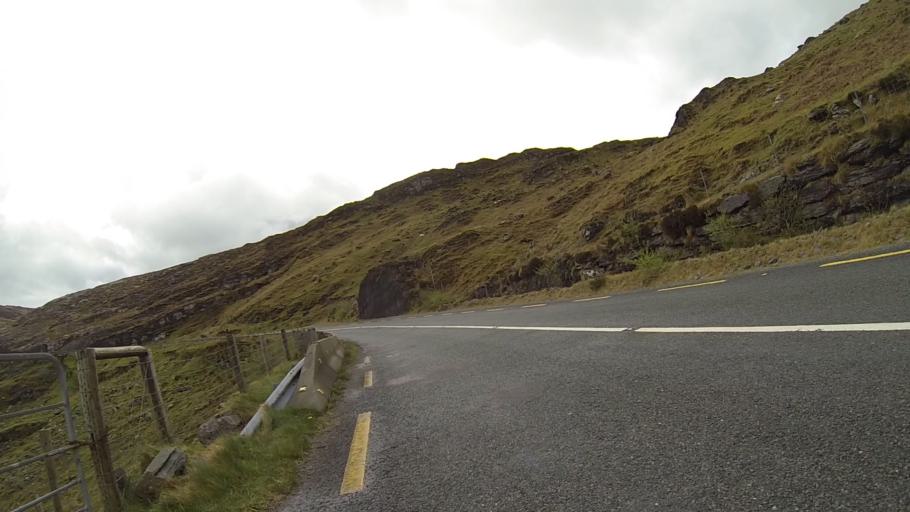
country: IE
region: Munster
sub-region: Ciarrai
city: Kenmare
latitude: 51.7876
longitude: -9.5928
